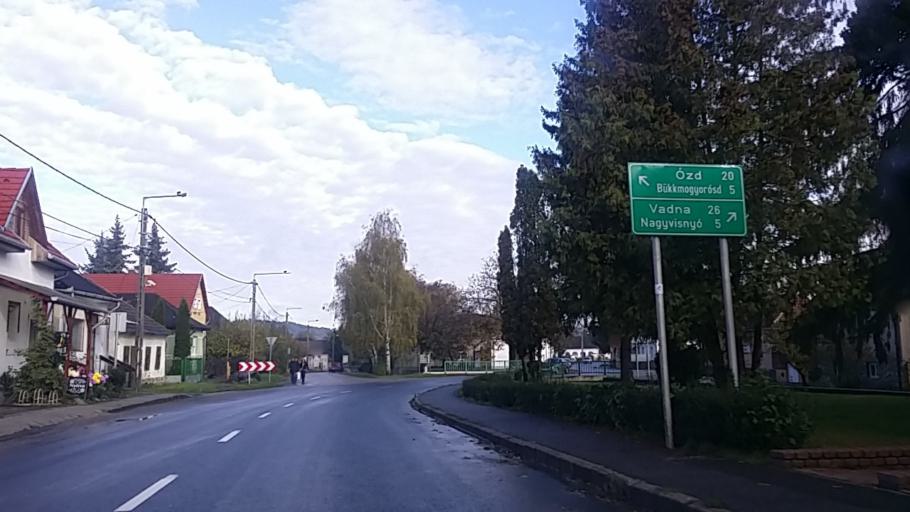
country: HU
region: Heves
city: Szilvasvarad
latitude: 48.1064
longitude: 20.3878
